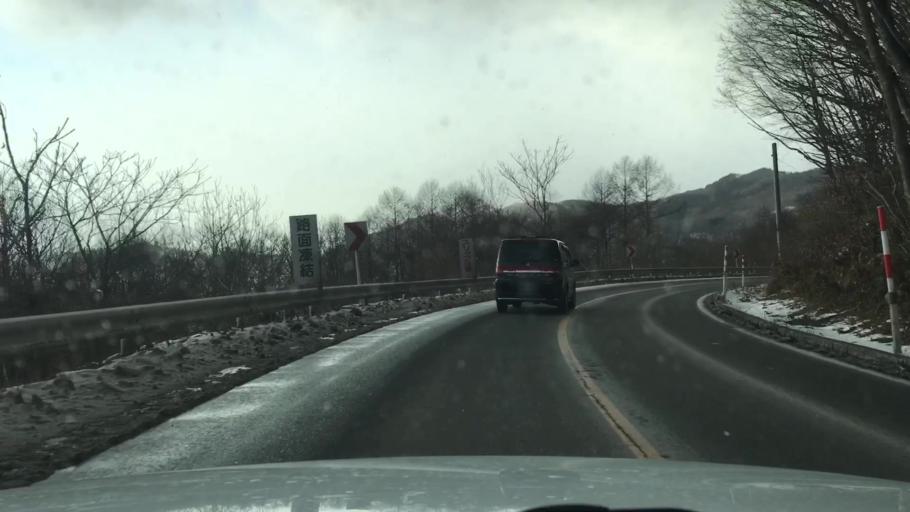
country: JP
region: Iwate
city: Morioka-shi
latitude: 39.6629
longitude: 141.3275
